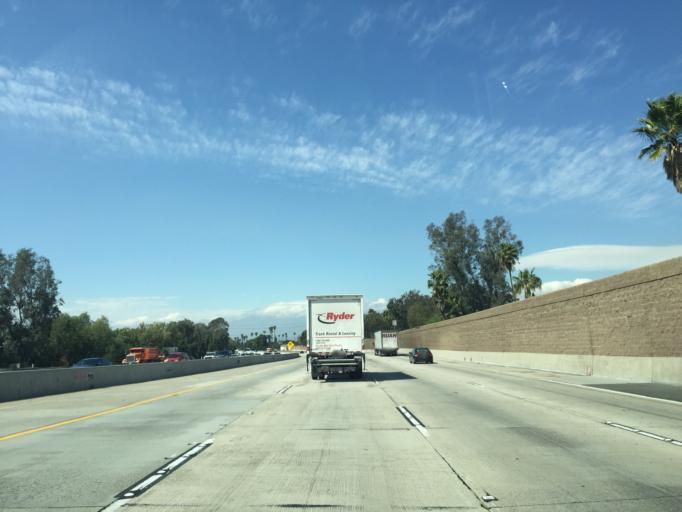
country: US
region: California
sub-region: San Bernardino County
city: Redlands
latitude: 34.0598
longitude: -117.1733
